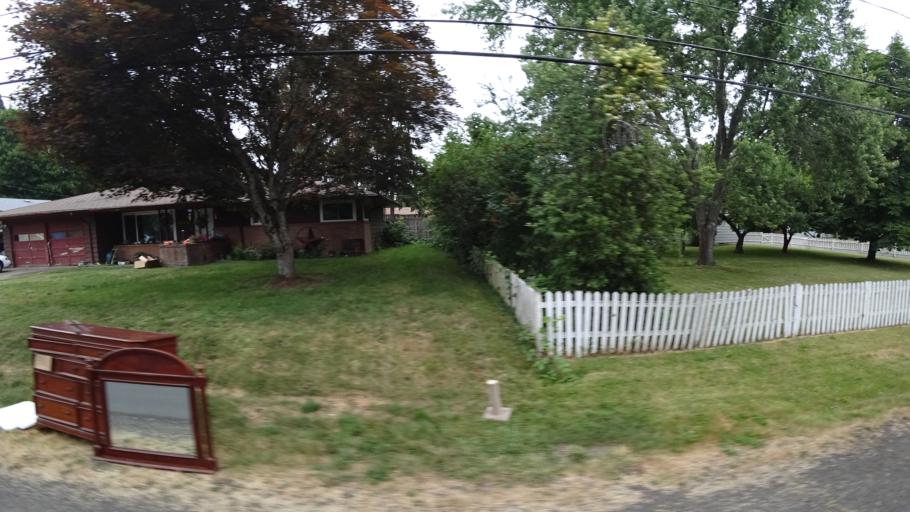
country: US
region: Oregon
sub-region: Washington County
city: Aloha
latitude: 45.5005
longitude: -122.8787
